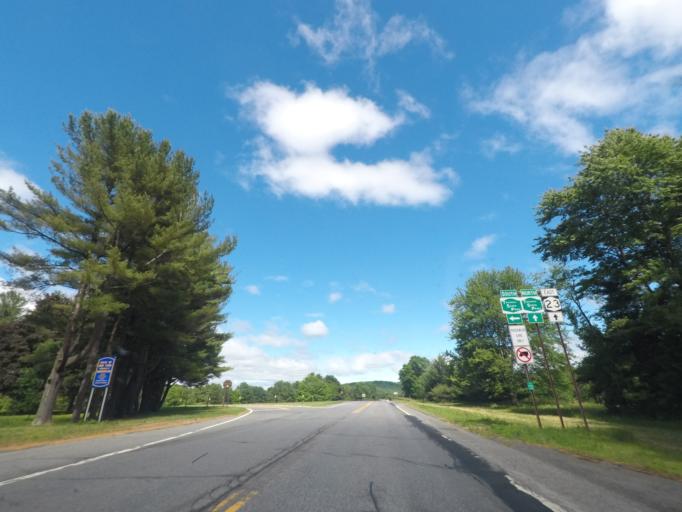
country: US
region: New York
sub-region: Columbia County
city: Philmont
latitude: 42.2091
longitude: -73.6398
